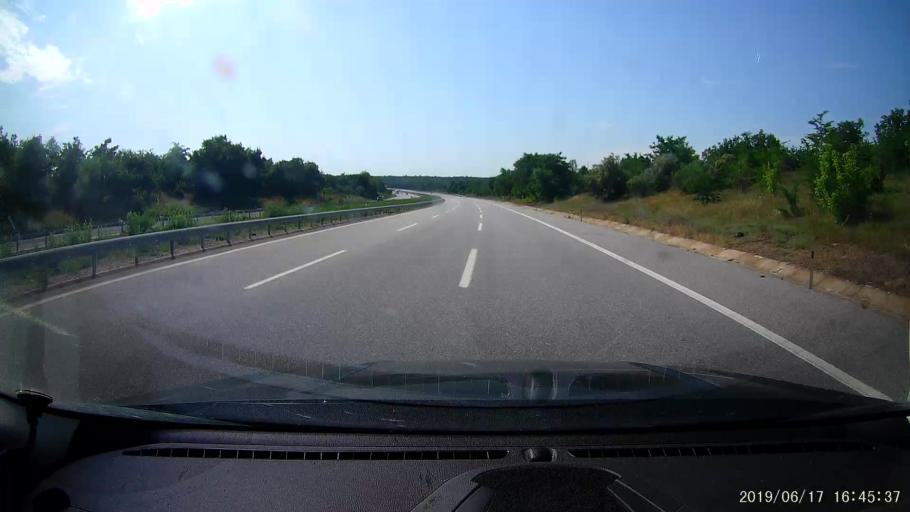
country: TR
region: Kirklareli
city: Babaeski
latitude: 41.4910
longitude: 27.2281
